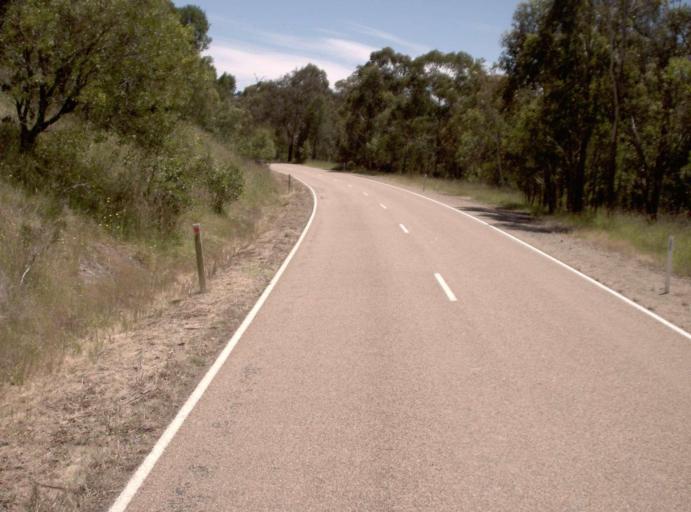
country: AU
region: Victoria
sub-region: East Gippsland
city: Lakes Entrance
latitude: -37.2119
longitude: 148.2691
